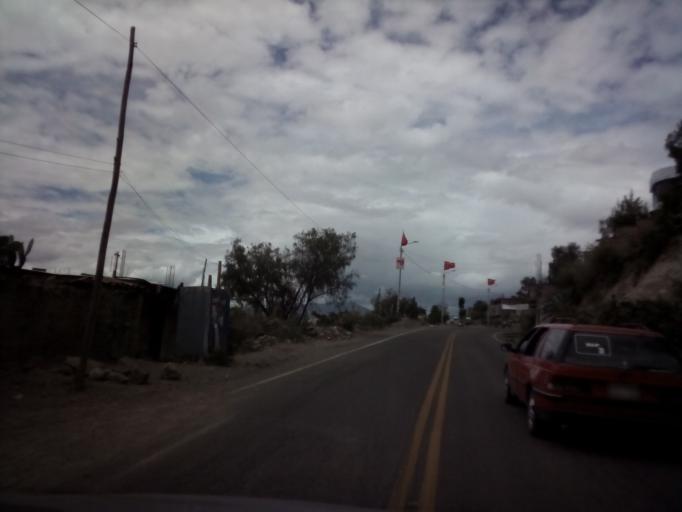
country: PE
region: Ayacucho
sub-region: Provincia de Huamanga
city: Ayacucho
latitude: -13.1636
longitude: -74.2406
